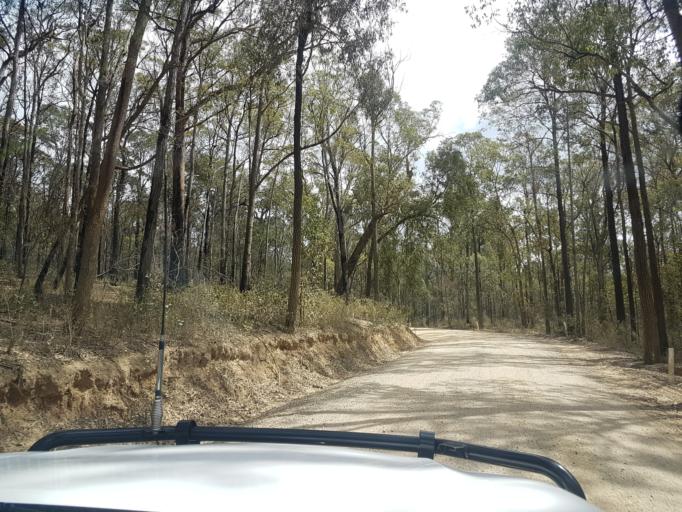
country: AU
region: Victoria
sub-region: East Gippsland
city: Bairnsdale
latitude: -37.7003
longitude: 147.5830
